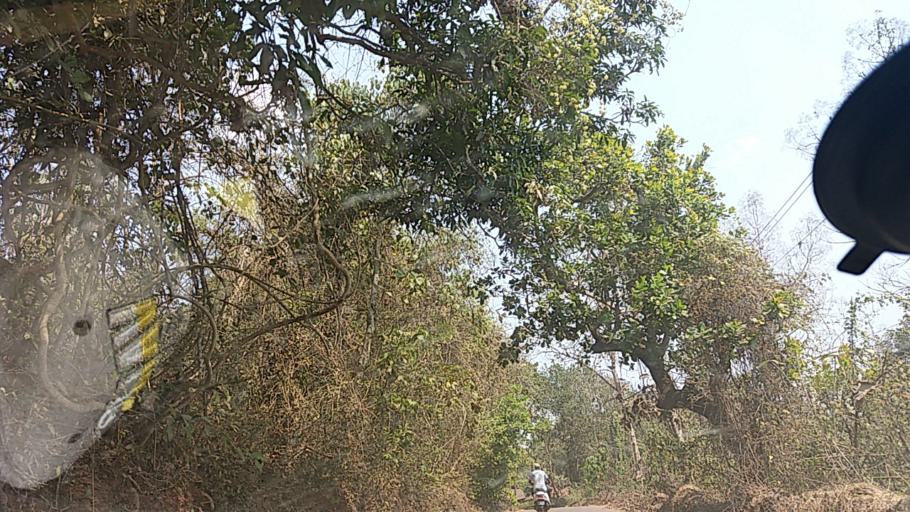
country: IN
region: Goa
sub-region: South Goa
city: Sancoale
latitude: 15.3685
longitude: 73.9161
